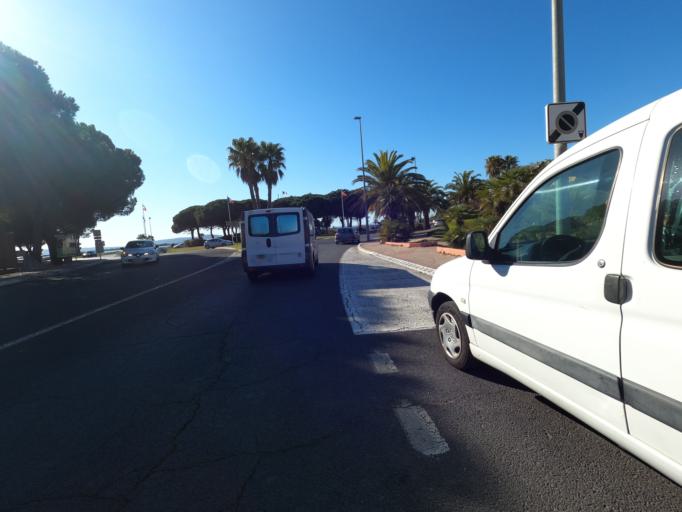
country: FR
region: Languedoc-Roussillon
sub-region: Departement de l'Herault
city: Palavas-les-Flots
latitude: 43.5296
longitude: 3.9240
